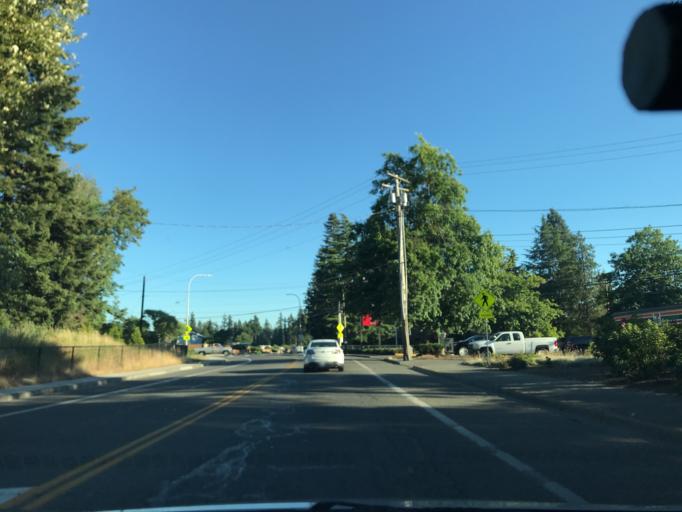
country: US
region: Washington
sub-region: King County
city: Auburn
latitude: 47.2911
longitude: -122.2082
